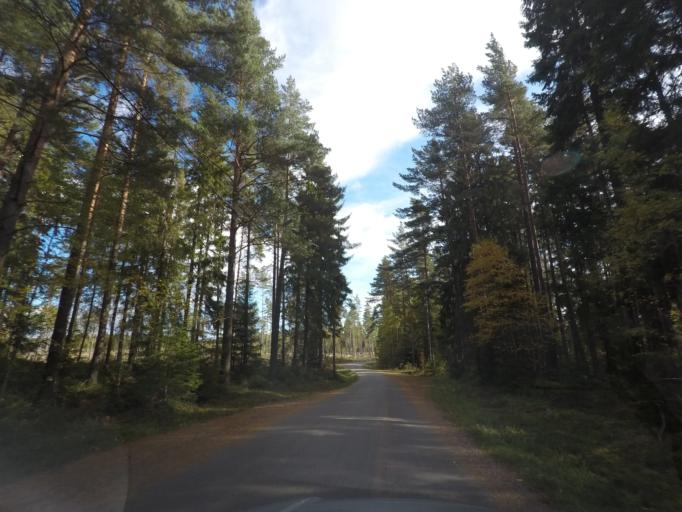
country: SE
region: Vaestmanland
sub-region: Kungsors Kommun
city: Kungsoer
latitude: 59.3384
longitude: 16.2066
